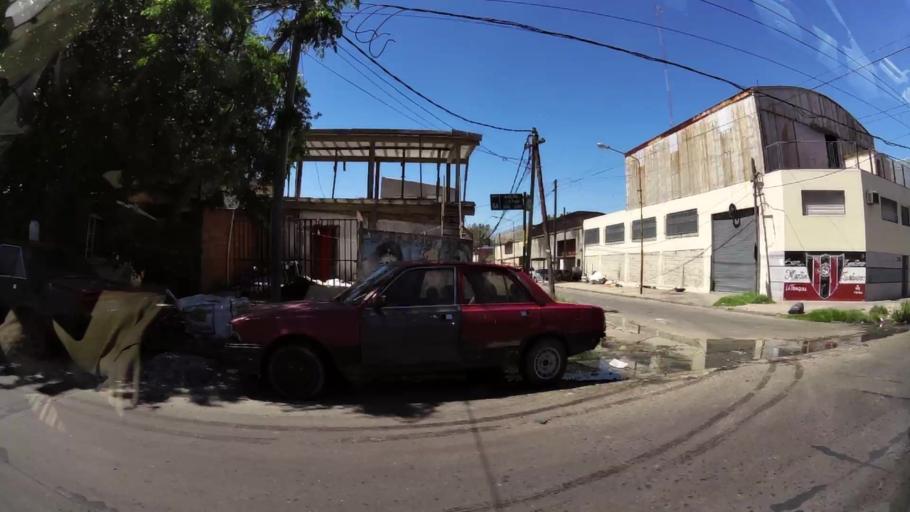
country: AR
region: Buenos Aires
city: Caseros
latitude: -34.5826
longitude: -58.5556
